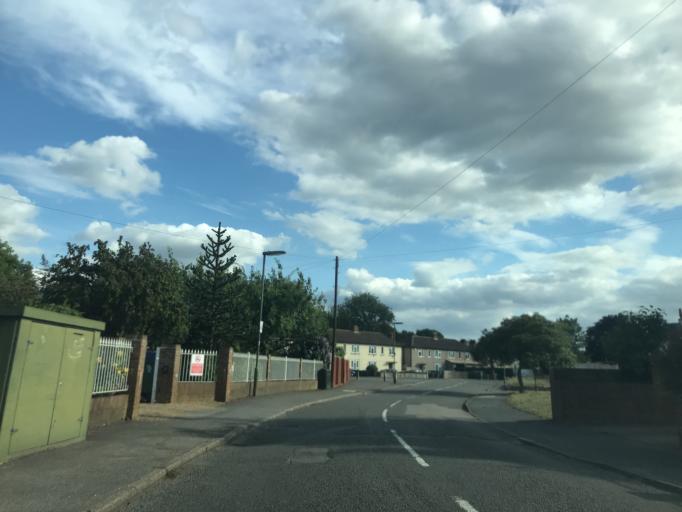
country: GB
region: England
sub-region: Surrey
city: Colnbrook
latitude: 51.4646
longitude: -0.5009
